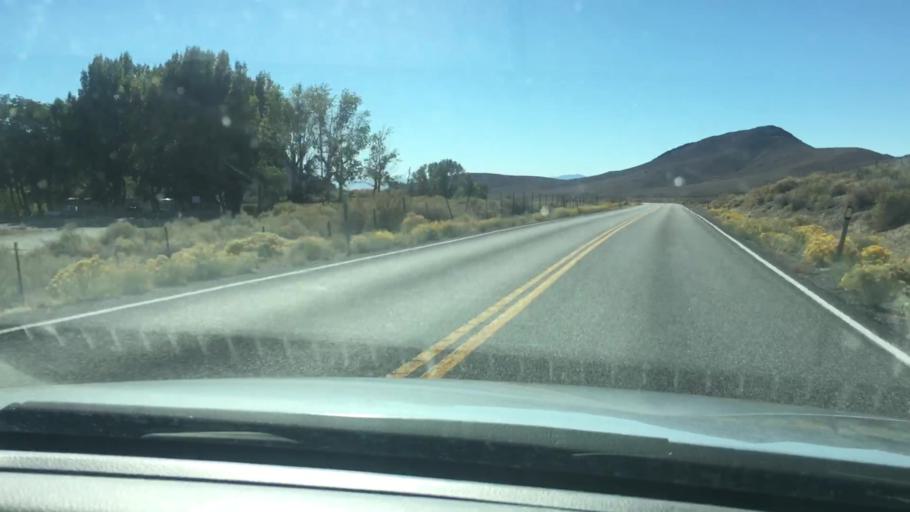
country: US
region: Nevada
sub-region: White Pine County
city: Ely
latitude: 38.7765
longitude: -115.4191
